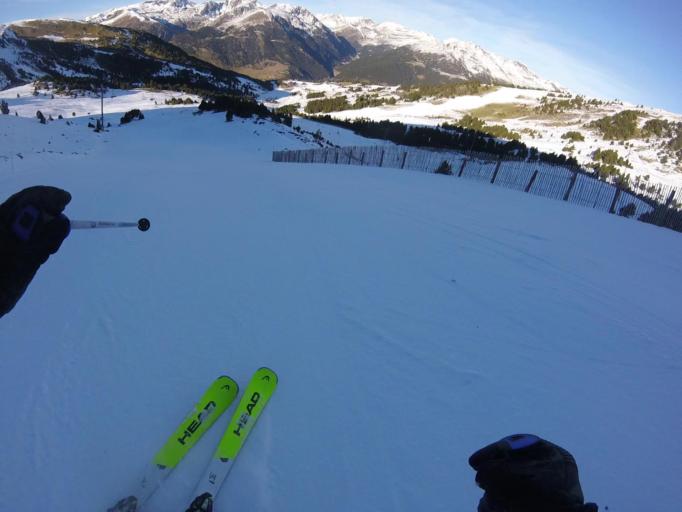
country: AD
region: Canillo
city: El Tarter
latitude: 42.5560
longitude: 1.6462
